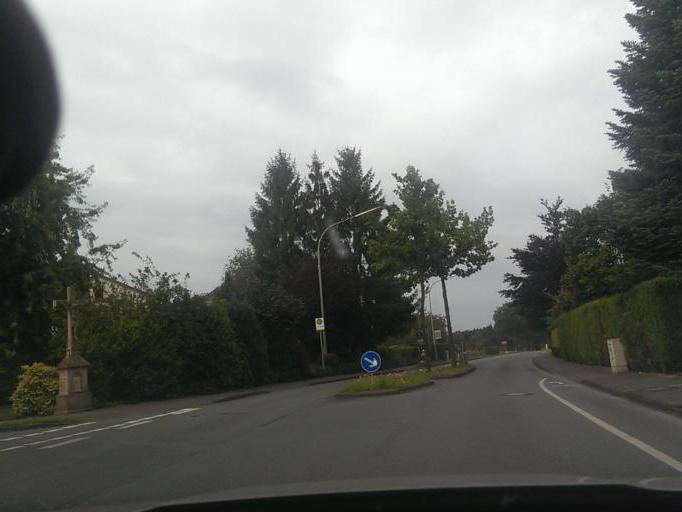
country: DE
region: North Rhine-Westphalia
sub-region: Regierungsbezirk Detmold
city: Delbruck
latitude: 51.7711
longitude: 8.5628
